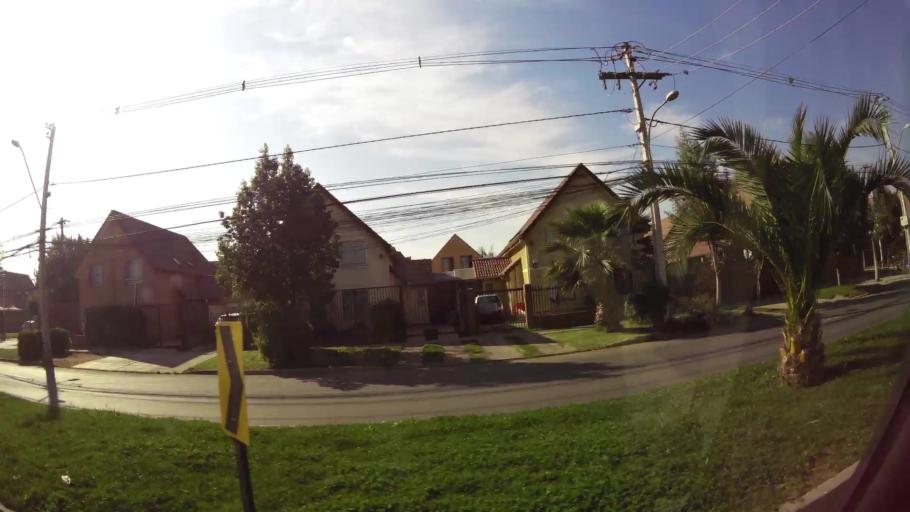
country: CL
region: Santiago Metropolitan
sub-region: Provincia de Santiago
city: Lo Prado
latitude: -33.4530
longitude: -70.7570
